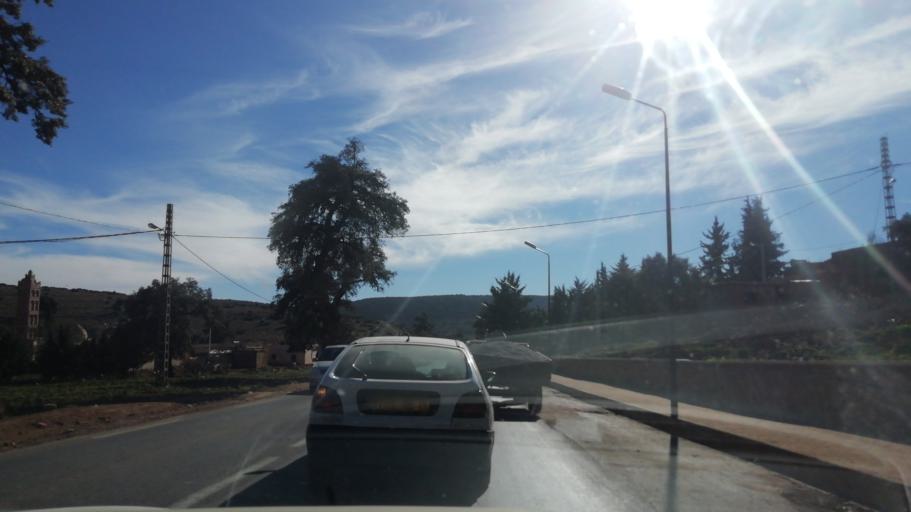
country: DZ
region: Tlemcen
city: Sebdou
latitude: 34.7266
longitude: -1.3373
